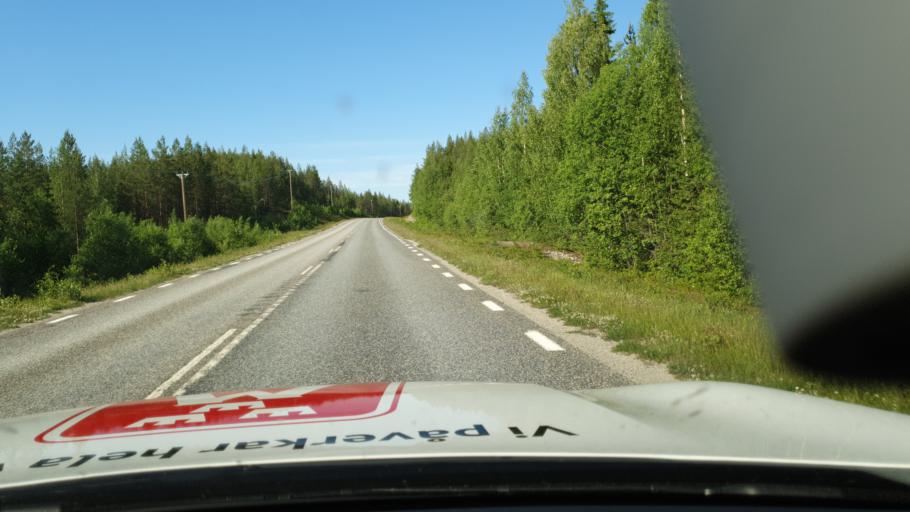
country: SE
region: Vaesterbotten
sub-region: Lycksele Kommun
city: Lycksele
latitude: 64.5704
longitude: 18.6170
